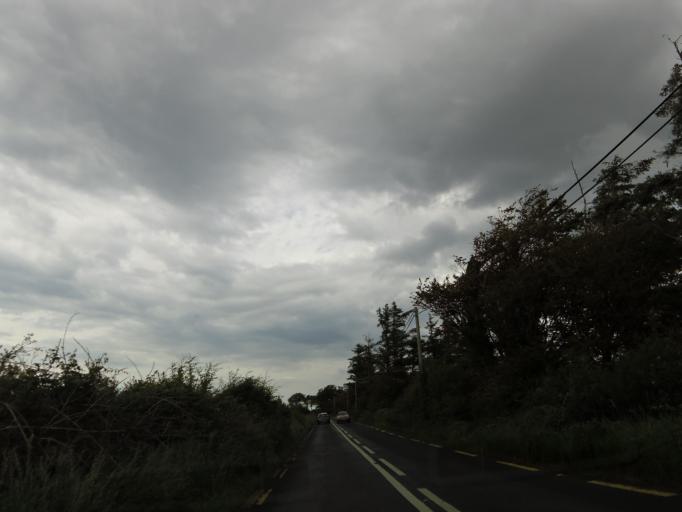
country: IE
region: Connaught
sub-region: County Galway
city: Gaillimh
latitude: 53.1336
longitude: -9.0668
